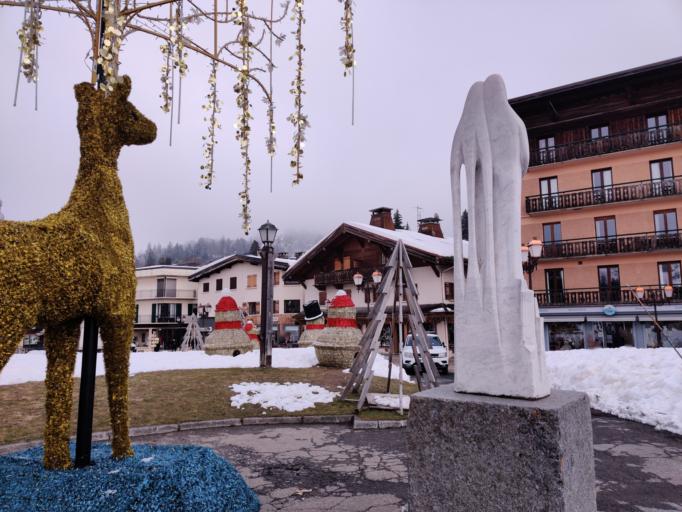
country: FR
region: Rhone-Alpes
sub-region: Departement de la Haute-Savoie
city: Megeve
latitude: 45.8557
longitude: 6.6167
